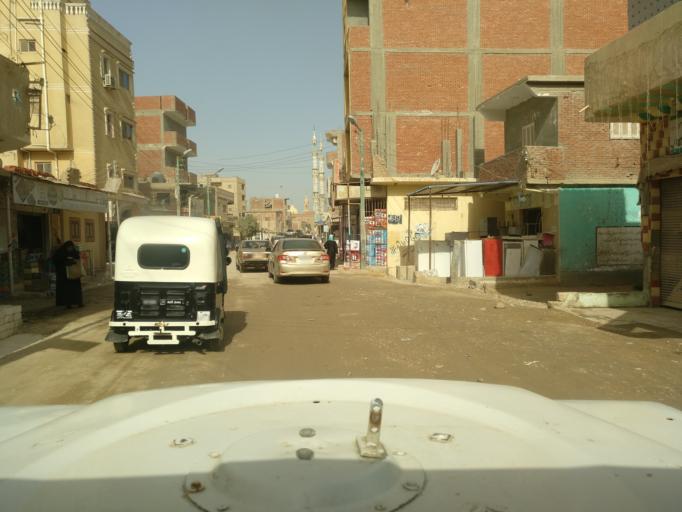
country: EG
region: Al Buhayrah
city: Beheira
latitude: 30.3741
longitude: 30.3508
